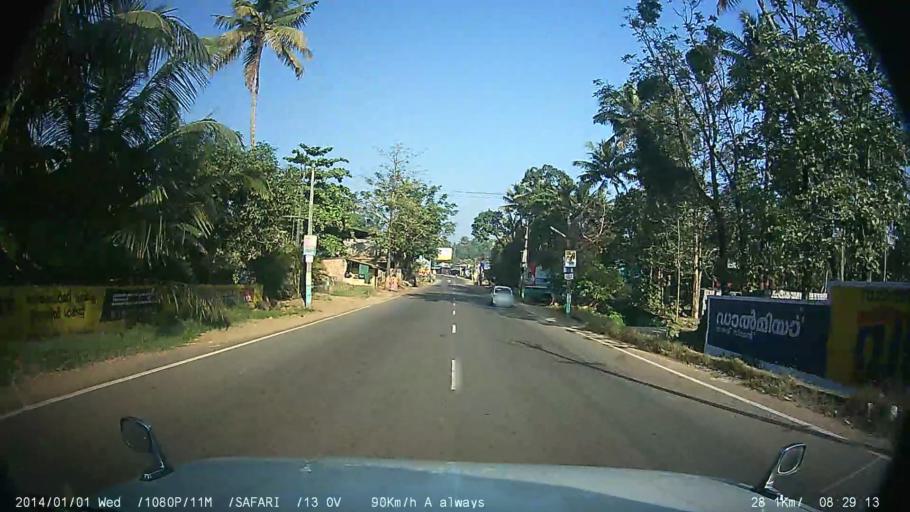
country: IN
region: Kerala
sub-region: Ernakulam
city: Perumbavoor
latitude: 10.0988
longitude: 76.4908
